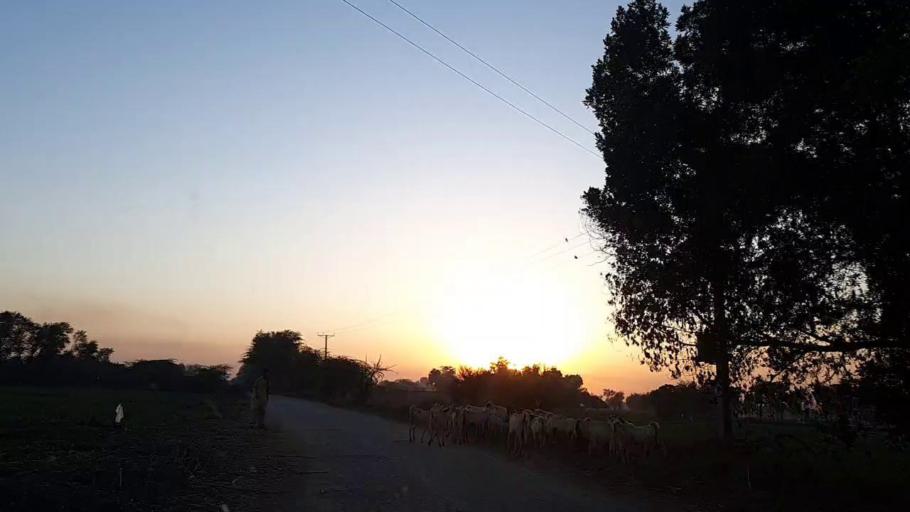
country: PK
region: Sindh
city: Daur
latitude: 26.3503
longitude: 68.3097
